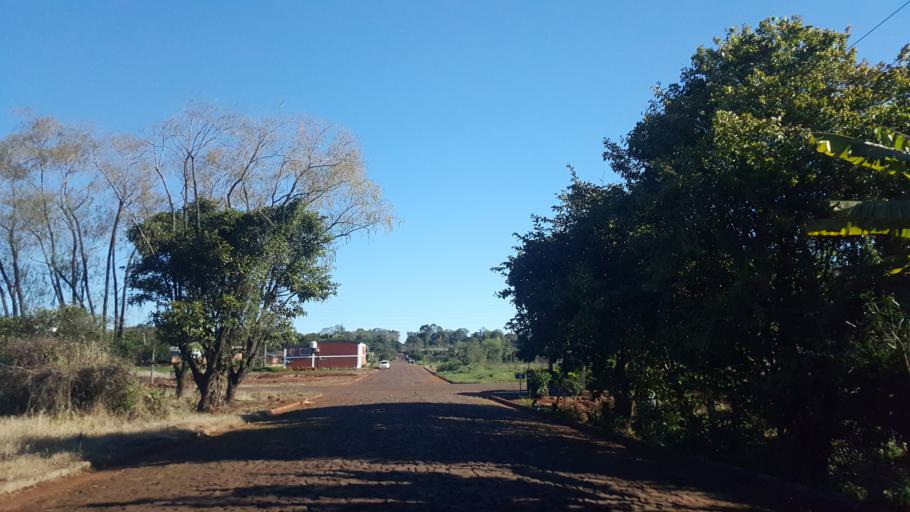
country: AR
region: Misiones
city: Gobernador Roca
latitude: -27.1849
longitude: -55.4645
